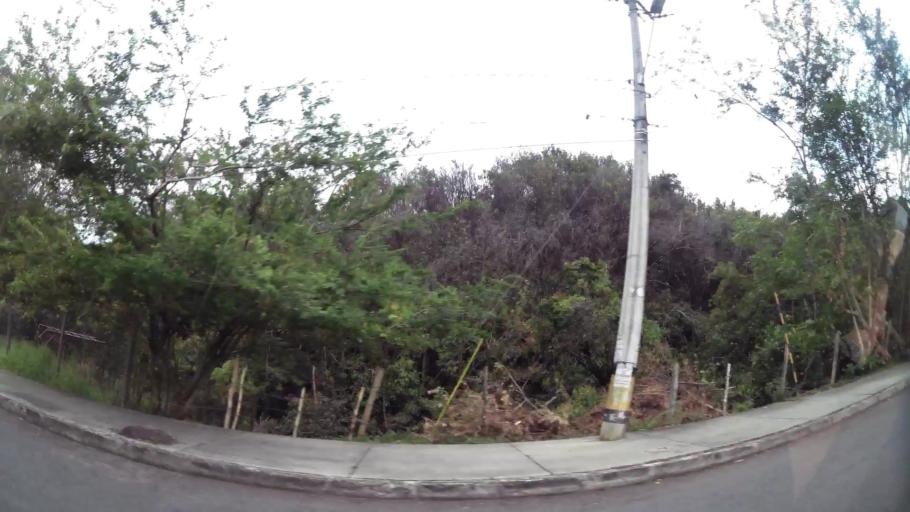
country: CO
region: Antioquia
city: Medellin
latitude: 6.2848
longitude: -75.5981
